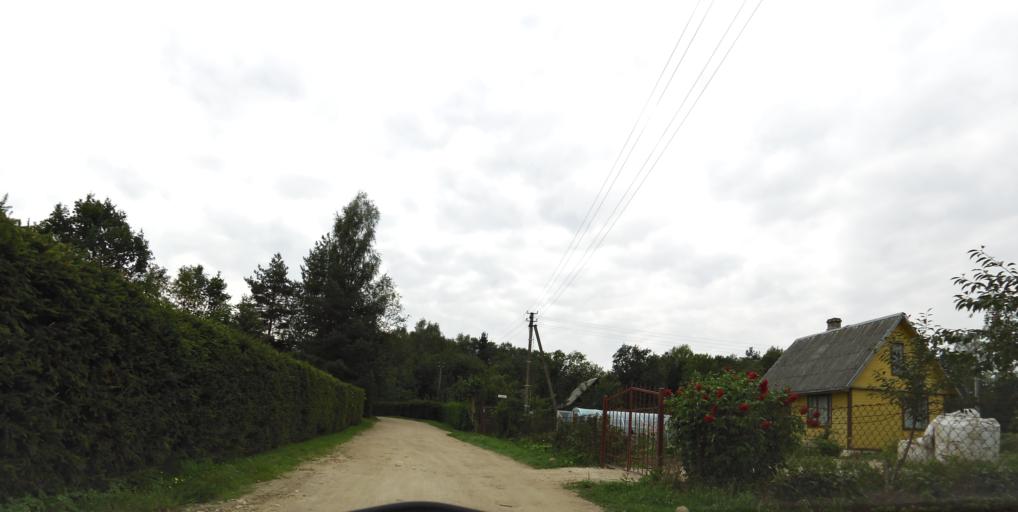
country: LT
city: Grigiskes
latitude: 54.7585
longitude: 25.0212
